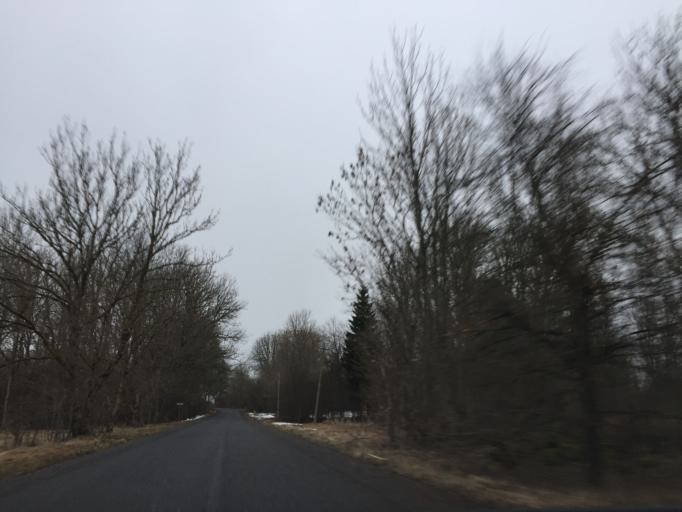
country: EE
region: Laeaene
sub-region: Lihula vald
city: Lihula
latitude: 58.6549
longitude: 23.6035
